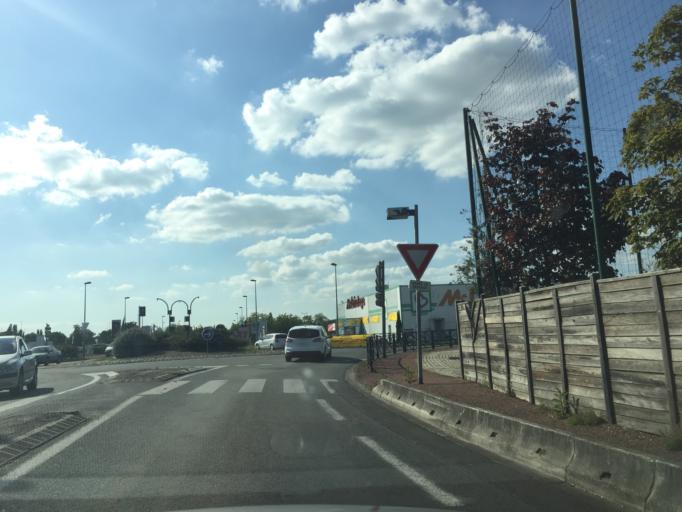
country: FR
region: Aquitaine
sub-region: Departement de la Gironde
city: Libourne
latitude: 44.8989
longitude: -0.2120
